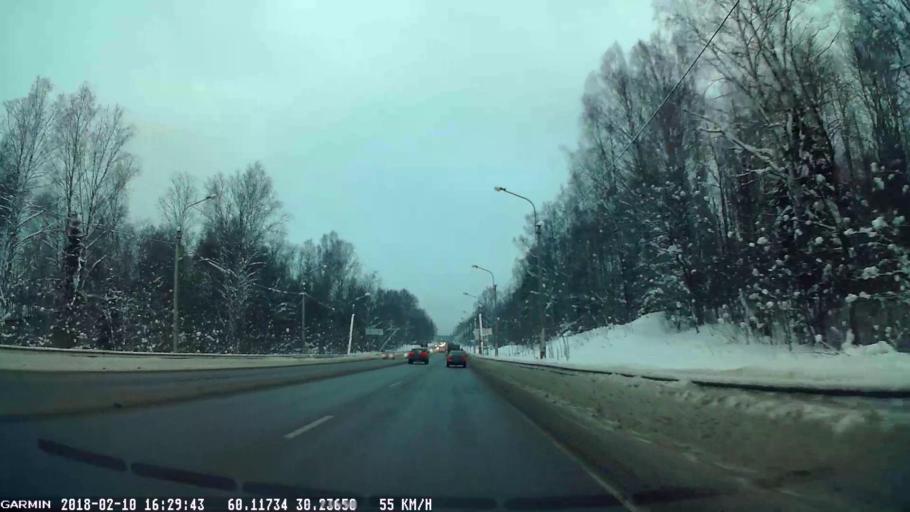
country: RU
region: St.-Petersburg
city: Levashovo
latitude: 60.1179
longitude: 30.2360
